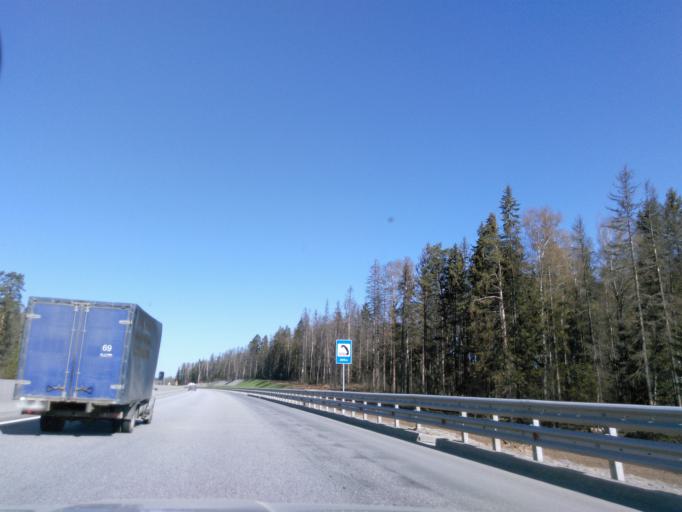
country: RU
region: Moskovskaya
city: Radumlya
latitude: 56.0914
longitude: 37.1976
